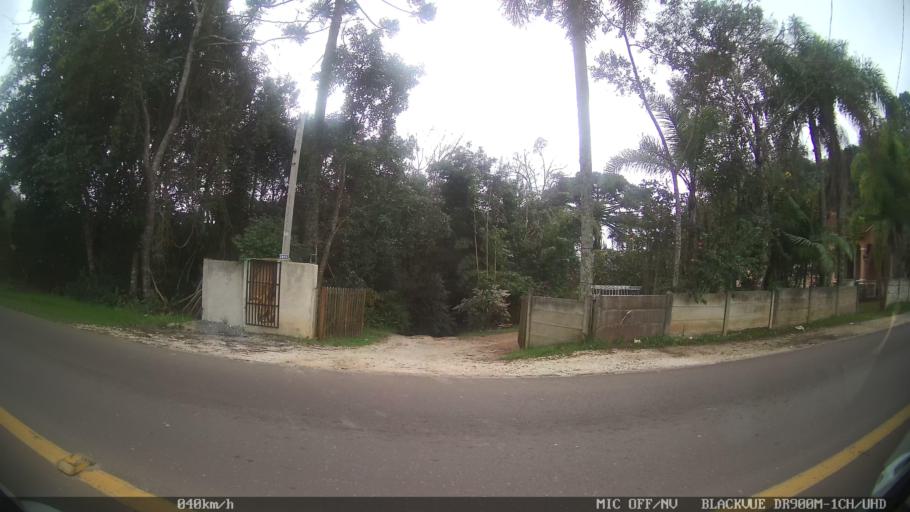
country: BR
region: Parana
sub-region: Curitiba
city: Curitiba
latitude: -25.3655
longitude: -49.2408
